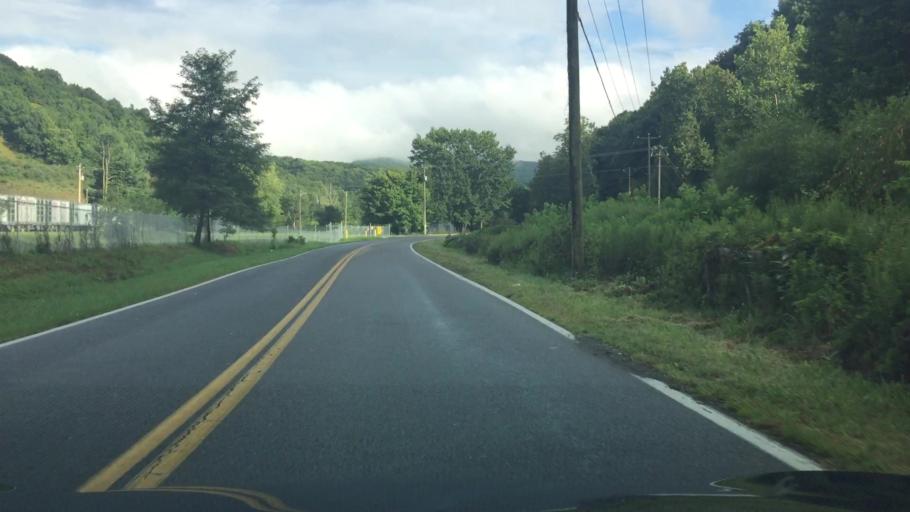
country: US
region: Virginia
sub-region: Smyth County
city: Atkins
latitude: 36.8577
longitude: -81.4311
